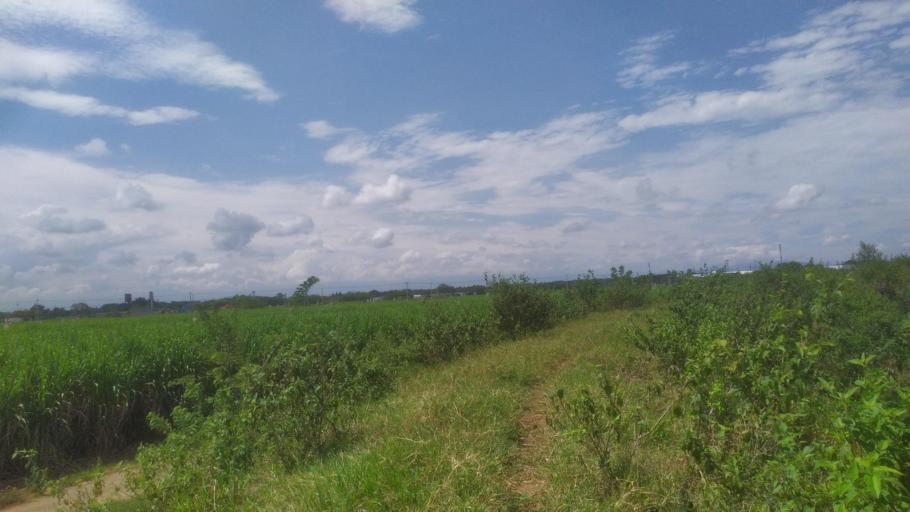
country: CO
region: Valle del Cauca
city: Jamundi
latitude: 3.2833
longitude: -76.5323
